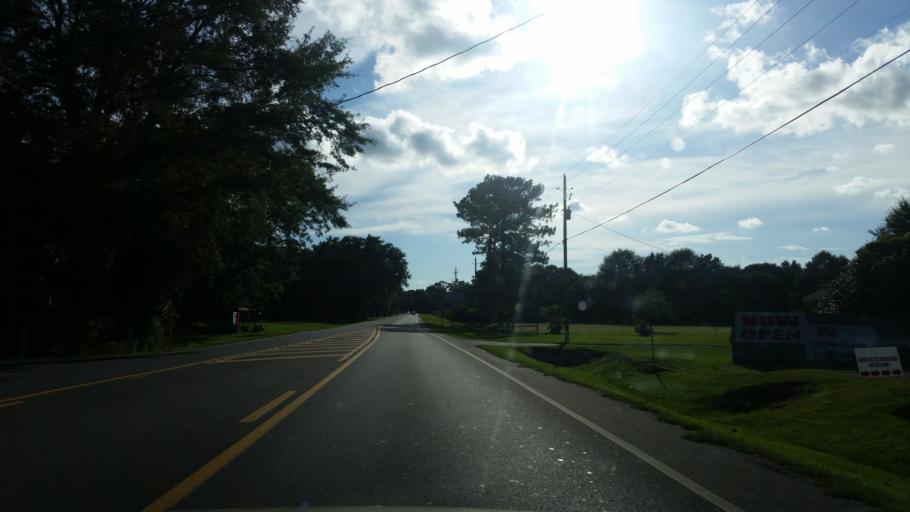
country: US
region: Alabama
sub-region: Baldwin County
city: Elberta
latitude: 30.4143
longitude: -87.6022
